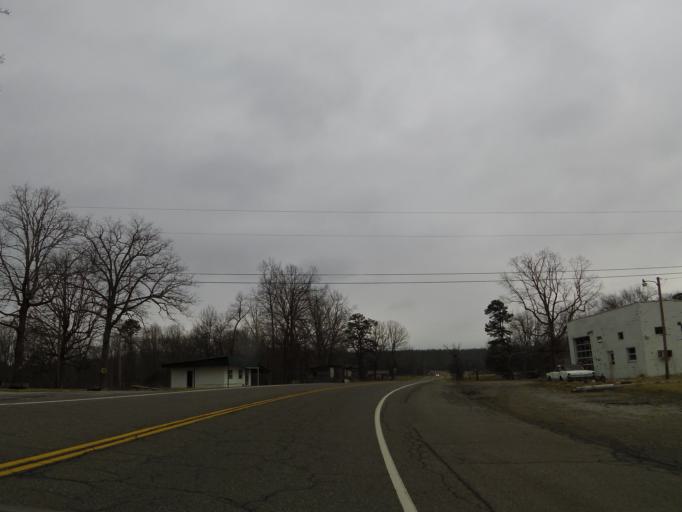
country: US
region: Tennessee
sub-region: Morgan County
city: Wartburg
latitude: 36.2894
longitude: -84.6585
